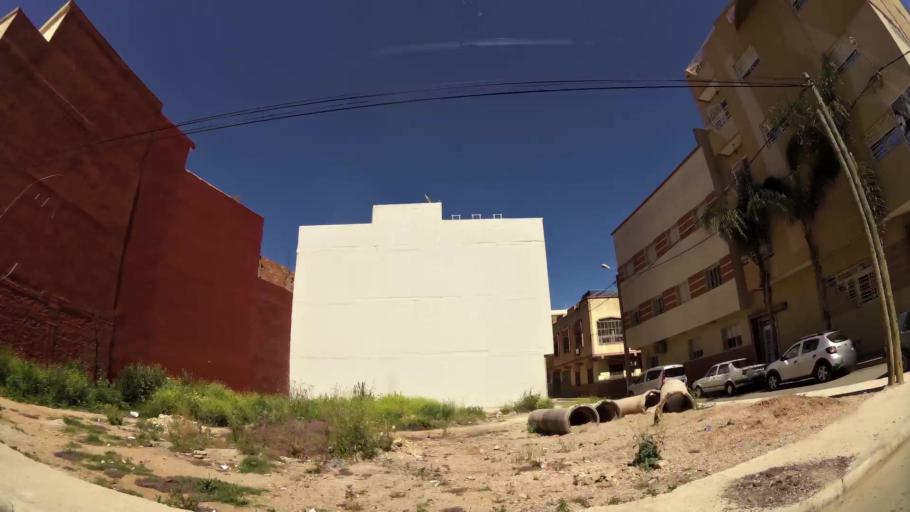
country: MA
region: Meknes-Tafilalet
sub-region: Meknes
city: Meknes
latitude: 33.8690
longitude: -5.5518
